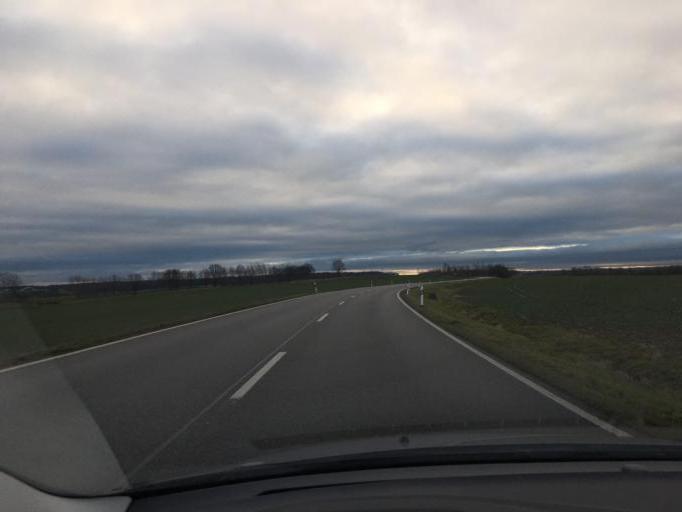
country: DE
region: Thuringia
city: Langenleuba-Niederhain
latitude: 50.9938
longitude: 12.6026
